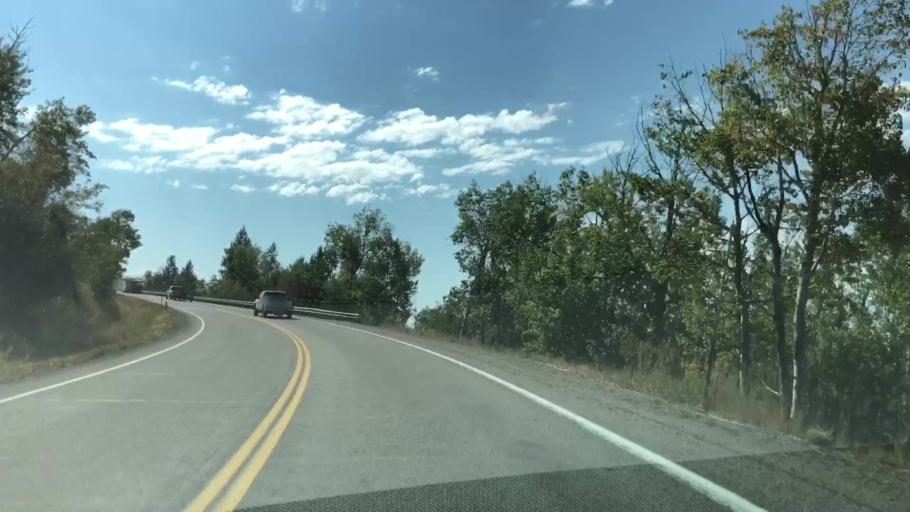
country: US
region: Idaho
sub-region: Teton County
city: Victor
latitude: 43.3138
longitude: -111.1465
